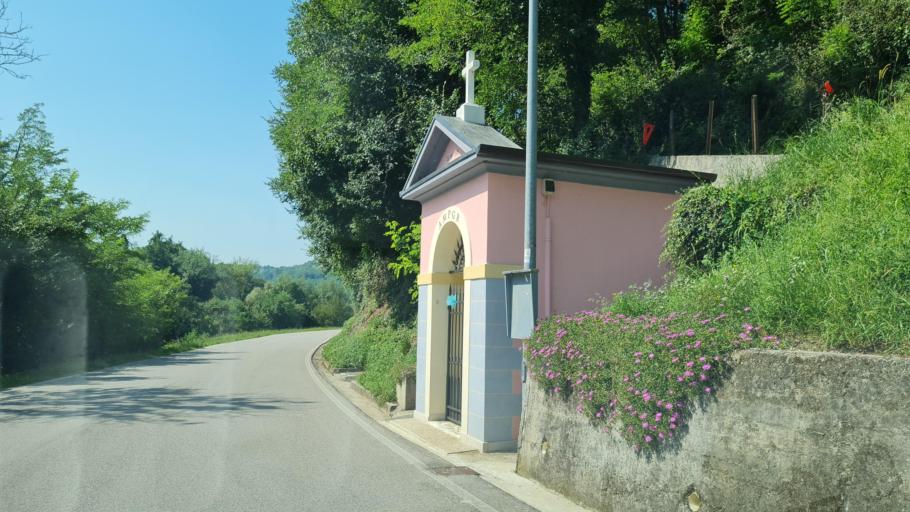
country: IT
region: Veneto
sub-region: Provincia di Vicenza
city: Salcedo
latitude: 45.7559
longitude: 11.5912
